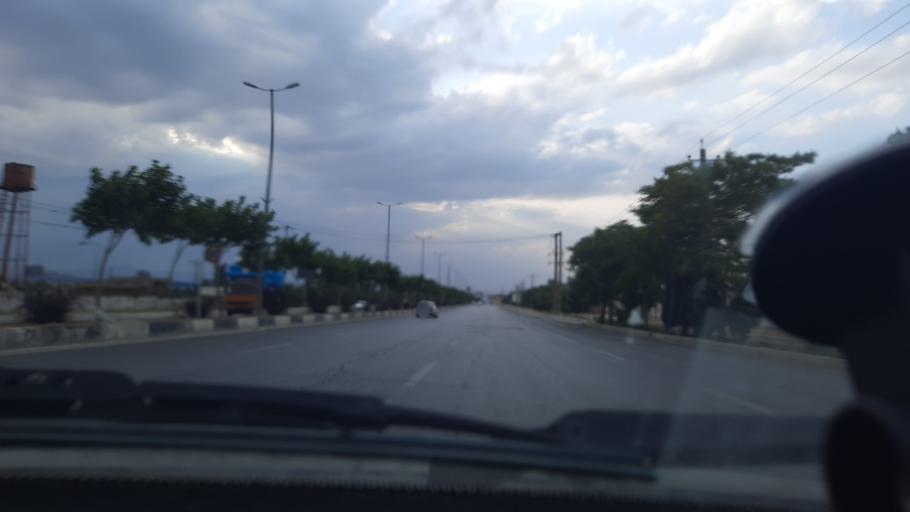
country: IR
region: Markazi
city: Arak
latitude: 34.0744
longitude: 49.7748
